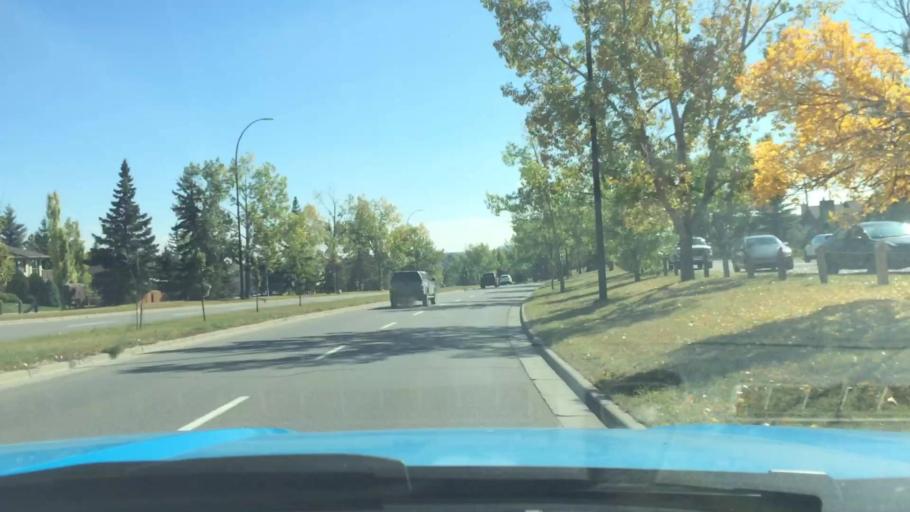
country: CA
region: Alberta
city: Calgary
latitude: 50.9138
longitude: -114.0797
